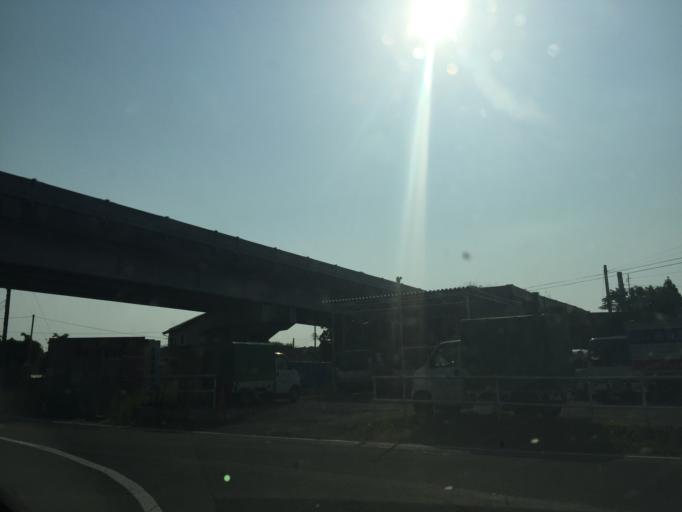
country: JP
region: Shizuoka
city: Kakegawa
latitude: 34.7868
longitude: 138.0229
